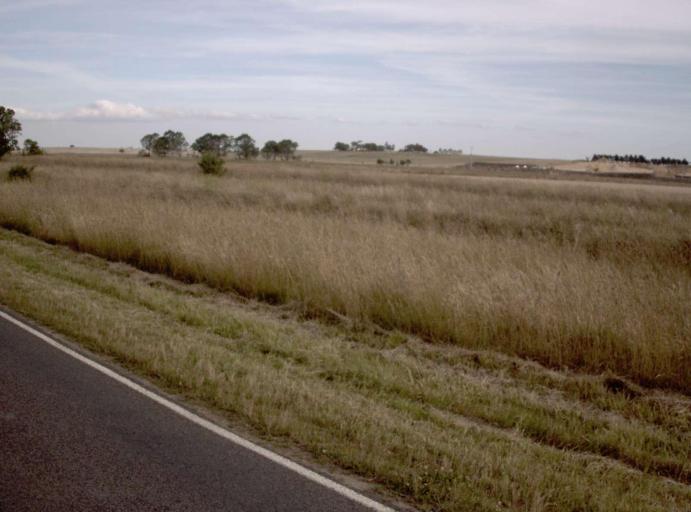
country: AU
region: Victoria
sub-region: Wellington
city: Heyfield
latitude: -38.0184
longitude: 146.7209
